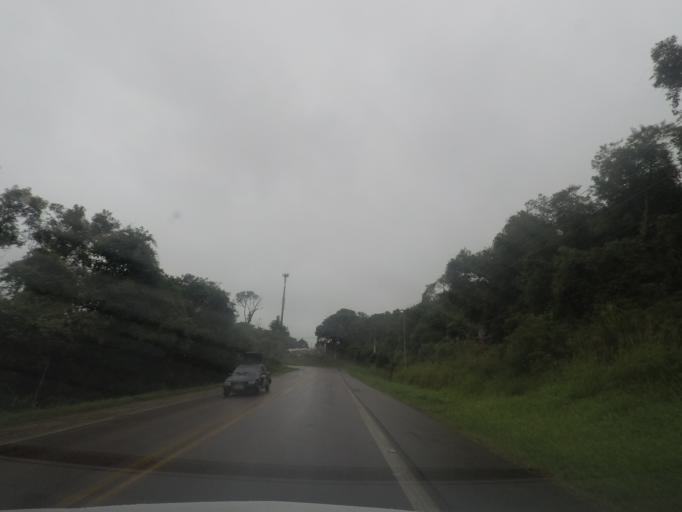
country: BR
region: Parana
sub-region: Colombo
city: Colombo
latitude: -25.3147
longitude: -49.1548
